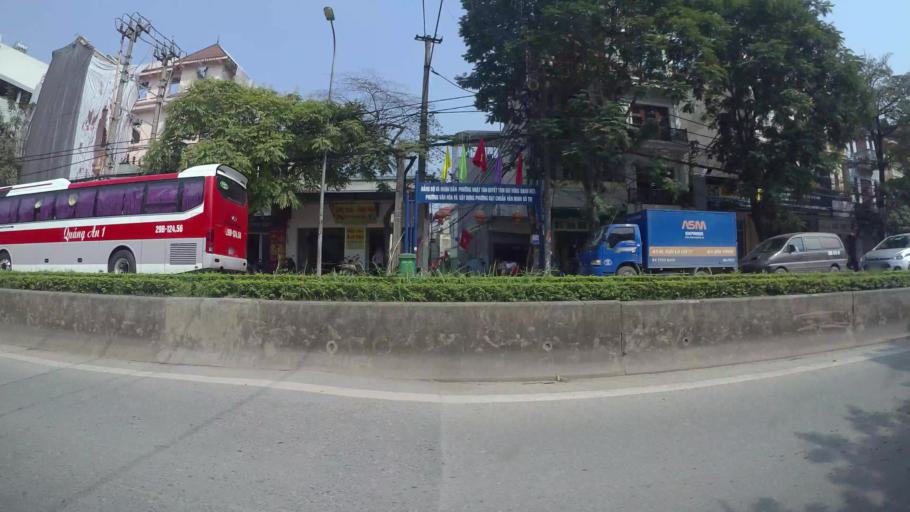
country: VN
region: Ha Noi
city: Tay Ho
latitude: 21.0785
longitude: 105.8159
